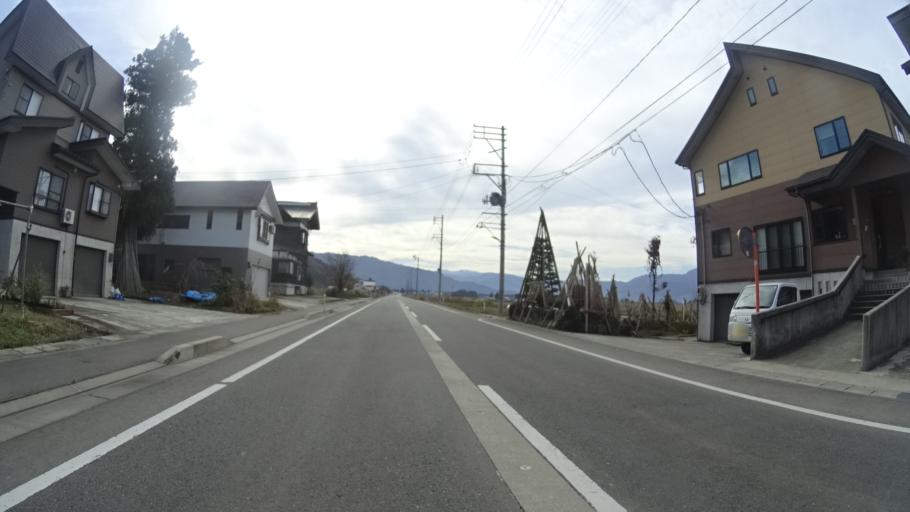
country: JP
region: Niigata
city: Muikamachi
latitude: 37.0383
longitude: 138.8912
